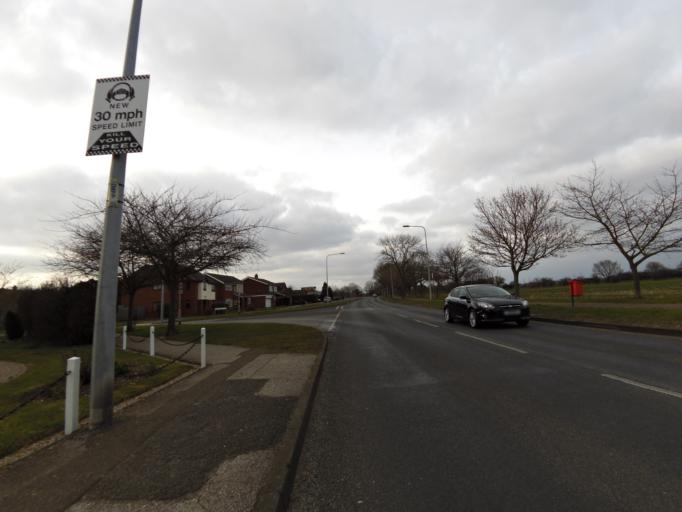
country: GB
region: England
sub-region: Suffolk
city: Ipswich
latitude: 52.0792
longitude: 1.1505
